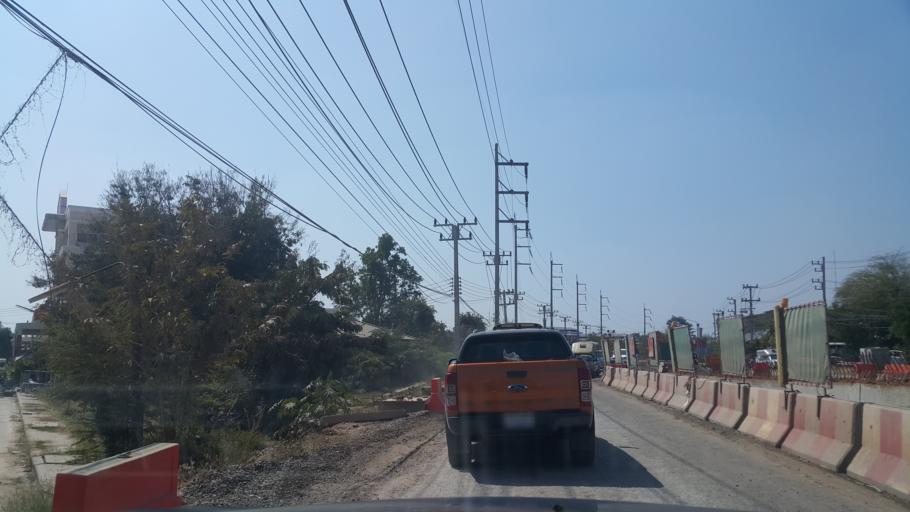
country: TH
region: Nakhon Ratchasima
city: Bua Yai
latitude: 15.5924
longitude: 102.4279
